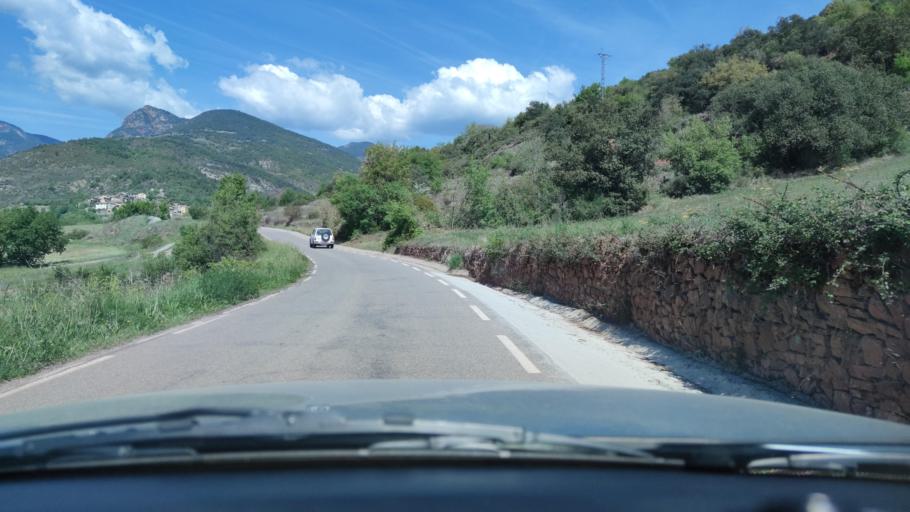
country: ES
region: Catalonia
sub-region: Provincia de Lleida
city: Coll de Nargo
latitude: 42.2905
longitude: 1.3566
